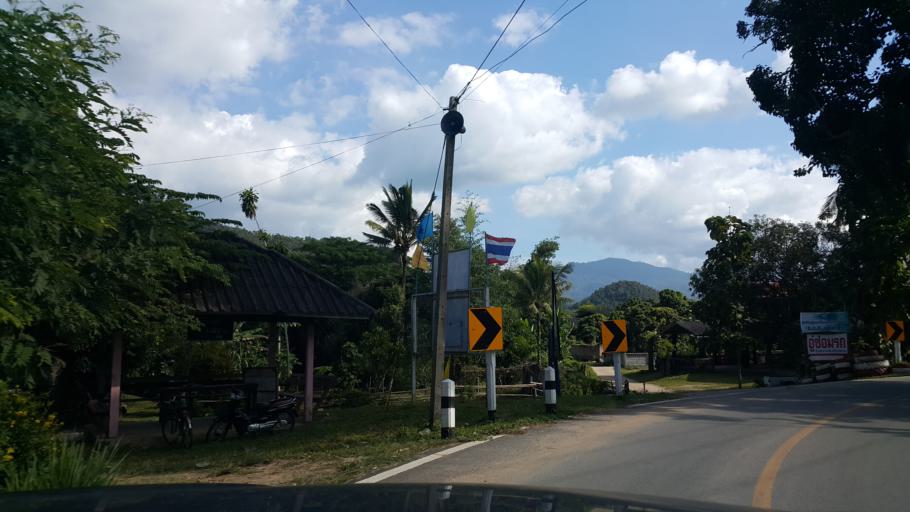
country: TH
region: Lamphun
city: Mae Tha
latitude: 18.5652
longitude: 99.2581
